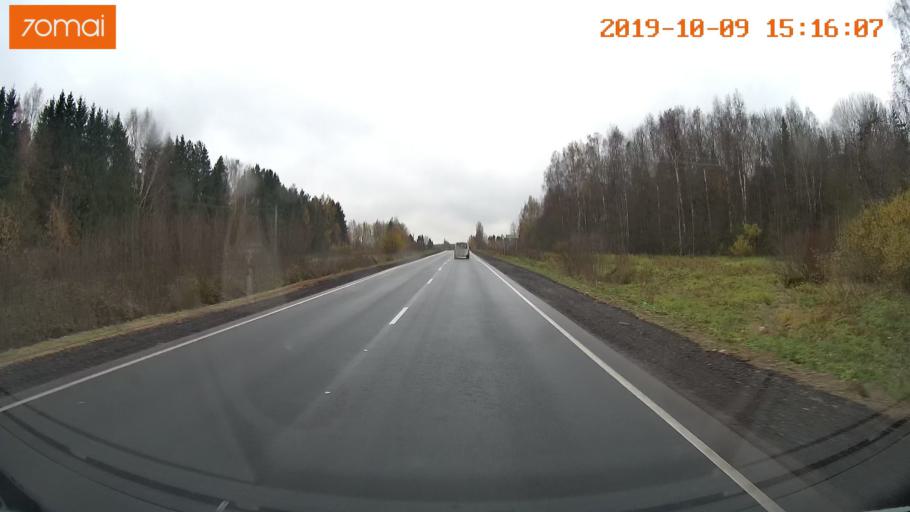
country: RU
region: Kostroma
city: Susanino
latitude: 58.1136
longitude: 41.5869
